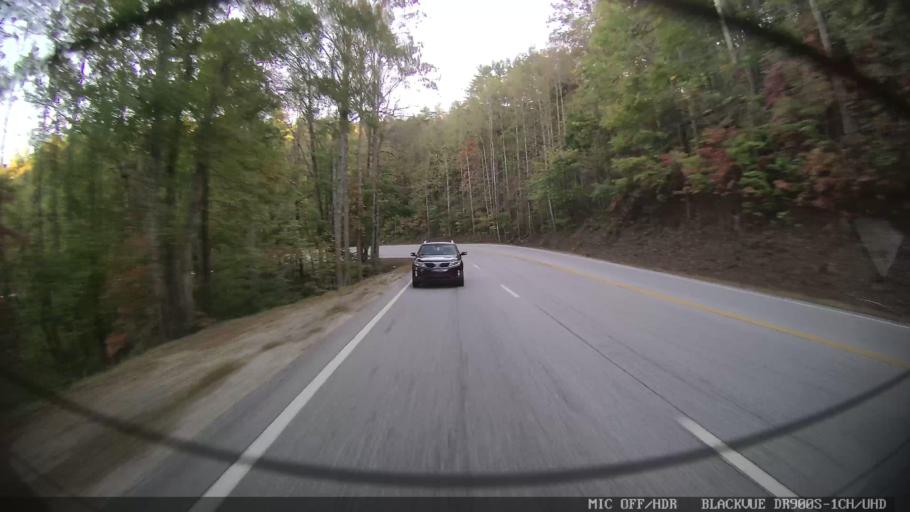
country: US
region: Georgia
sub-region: White County
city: Cleveland
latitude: 34.6853
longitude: -83.9058
